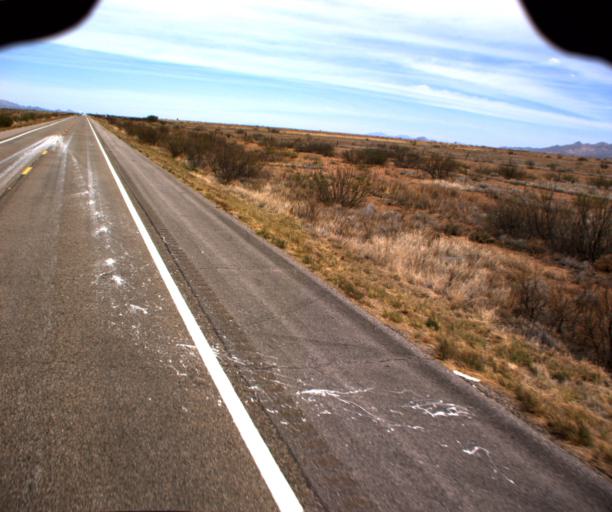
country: US
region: Arizona
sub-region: Cochise County
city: Pirtleville
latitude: 31.5092
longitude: -109.6399
